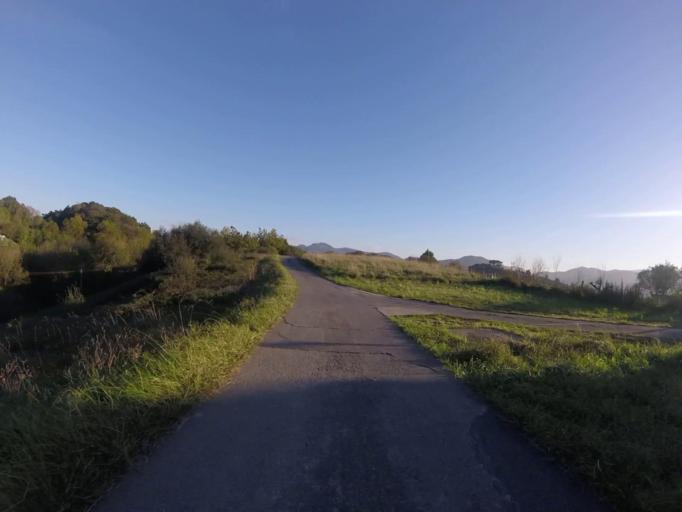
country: ES
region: Basque Country
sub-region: Provincia de Guipuzcoa
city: Lasarte
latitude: 43.2833
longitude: -2.0102
